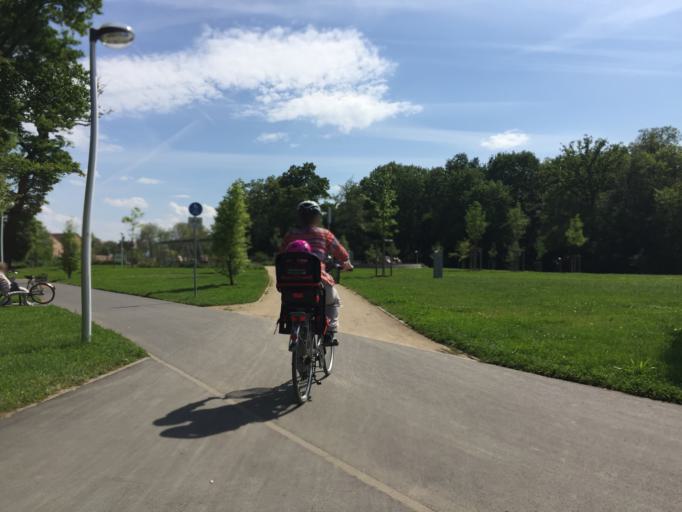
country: DE
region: Bavaria
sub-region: Regierungsbezirk Unterfranken
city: Aschaffenburg
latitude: 49.9780
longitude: 9.1609
